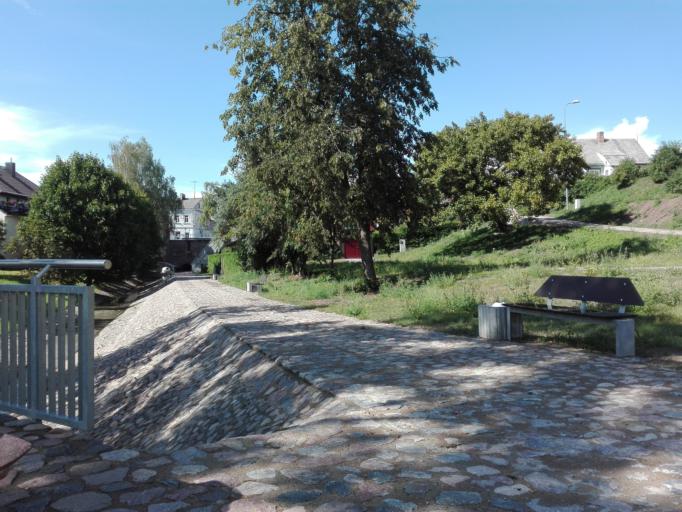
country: LT
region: Vilnius County
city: Ukmerge
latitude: 55.2501
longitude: 24.7685
